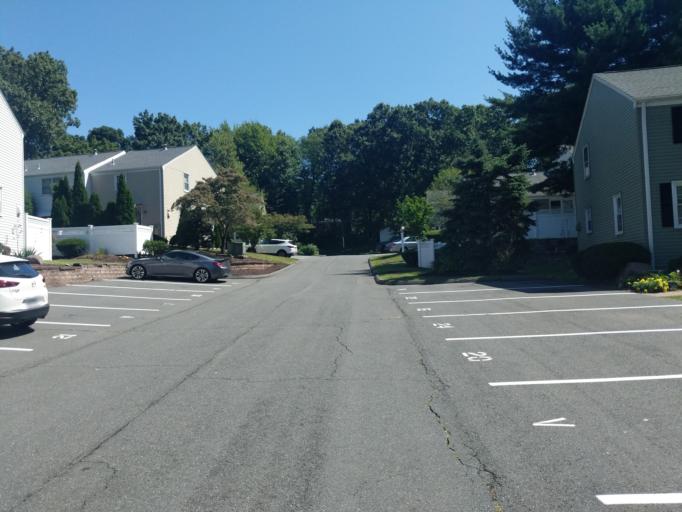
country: US
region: Connecticut
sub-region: Hartford County
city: Glastonbury
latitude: 41.7248
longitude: -72.5930
